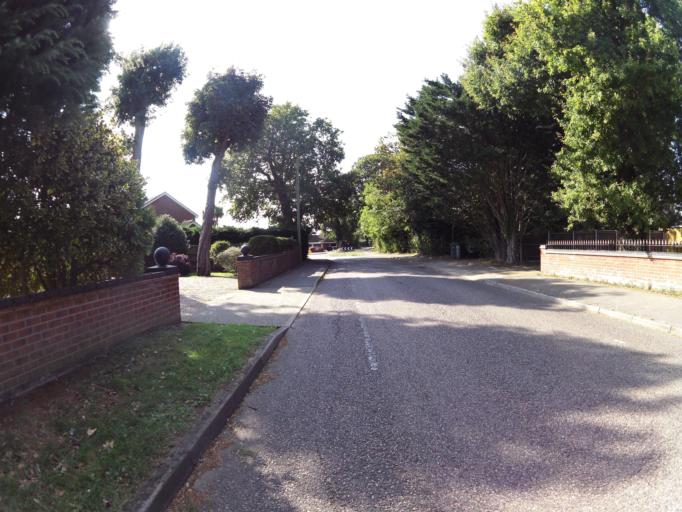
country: GB
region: England
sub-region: Suffolk
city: Kessingland
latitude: 52.4609
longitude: 1.7063
